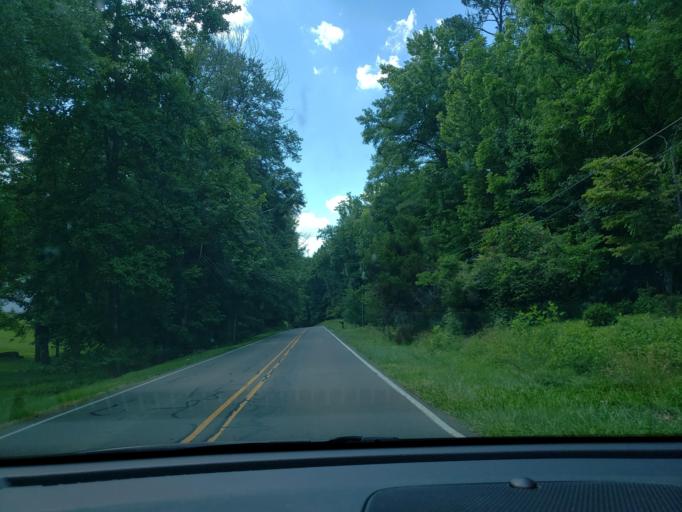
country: US
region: North Carolina
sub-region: Orange County
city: Chapel Hill
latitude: 35.9915
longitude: -78.9995
